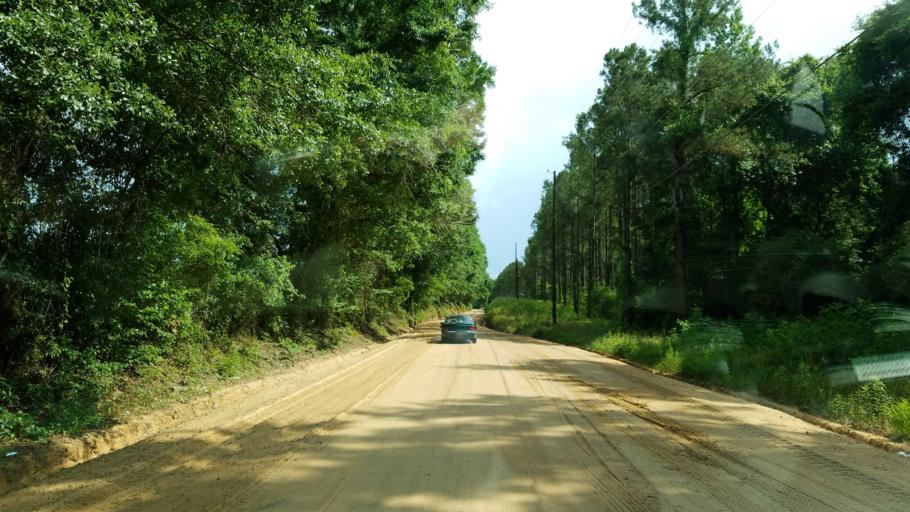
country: US
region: Georgia
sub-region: Houston County
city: Perry
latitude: 32.4432
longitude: -83.7891
